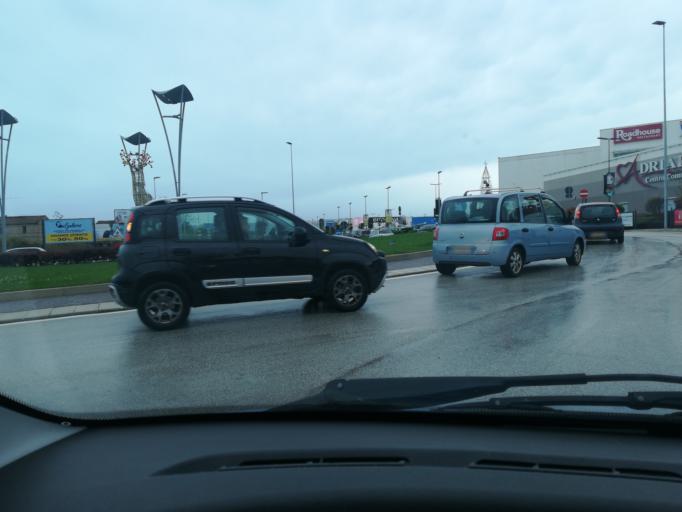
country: IT
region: The Marches
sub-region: Provincia di Macerata
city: Santa Maria Apparente
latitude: 43.2943
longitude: 13.7024
